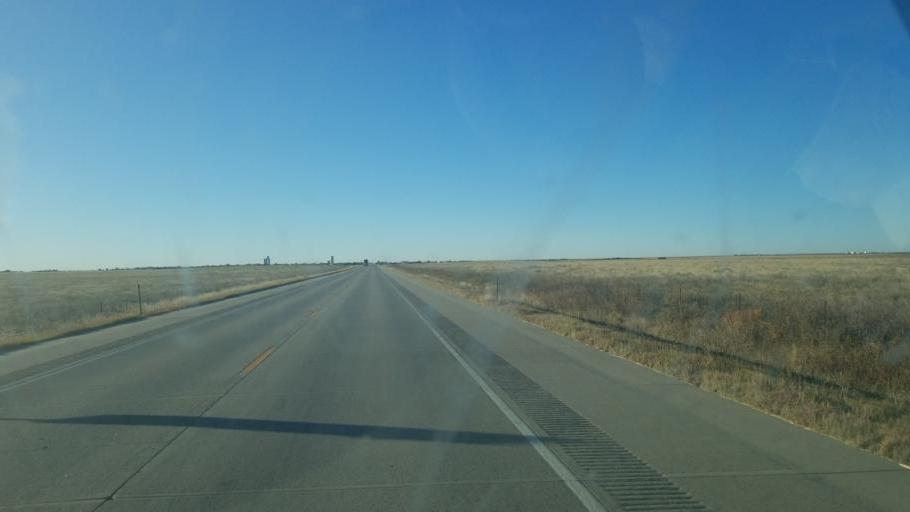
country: US
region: Colorado
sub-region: Kiowa County
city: Eads
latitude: 38.5097
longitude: -102.7857
